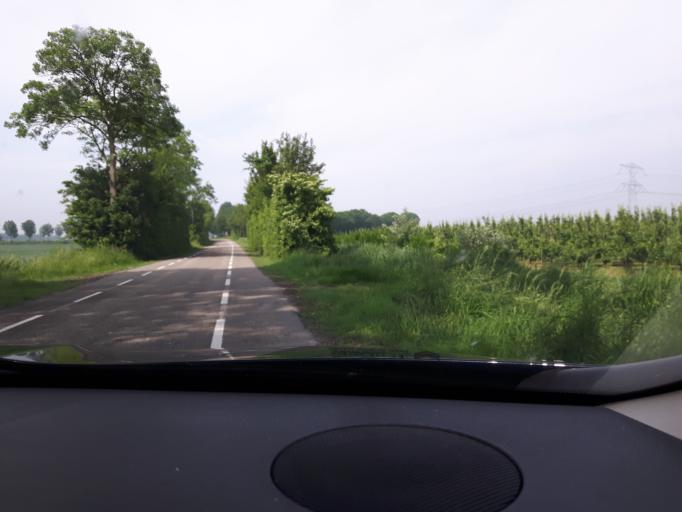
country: NL
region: Zeeland
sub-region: Gemeente Goes
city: Goes
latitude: 51.4268
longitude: 3.8860
